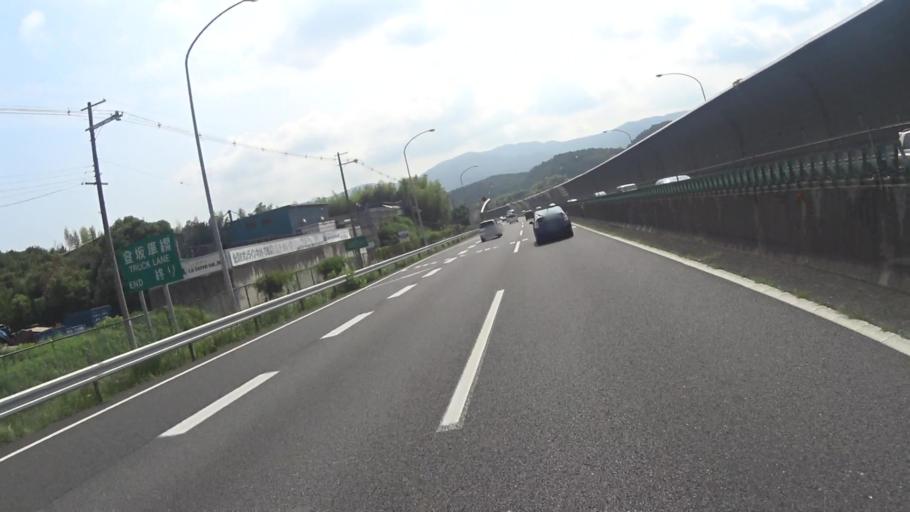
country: JP
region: Kyoto
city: Uji
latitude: 34.9568
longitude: 135.7913
